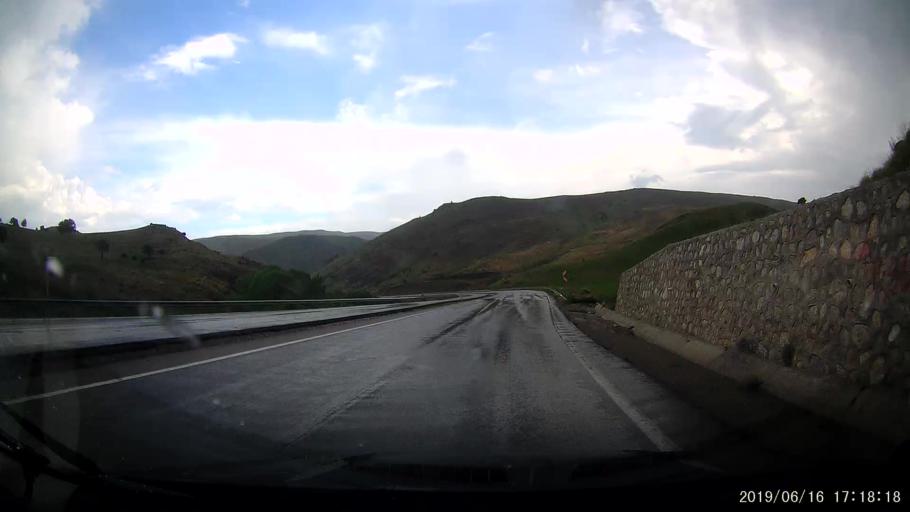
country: TR
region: Erzincan
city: Tercan
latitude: 39.8159
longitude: 40.5292
